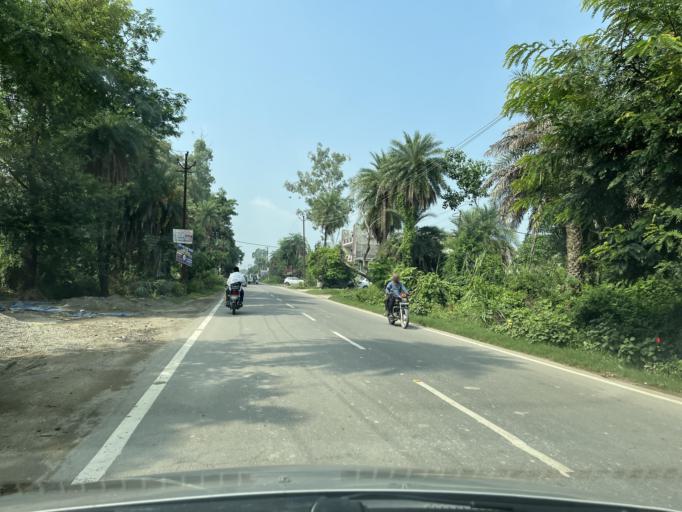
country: IN
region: Uttarakhand
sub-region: Udham Singh Nagar
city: Bazpur
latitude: 29.1689
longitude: 79.1637
